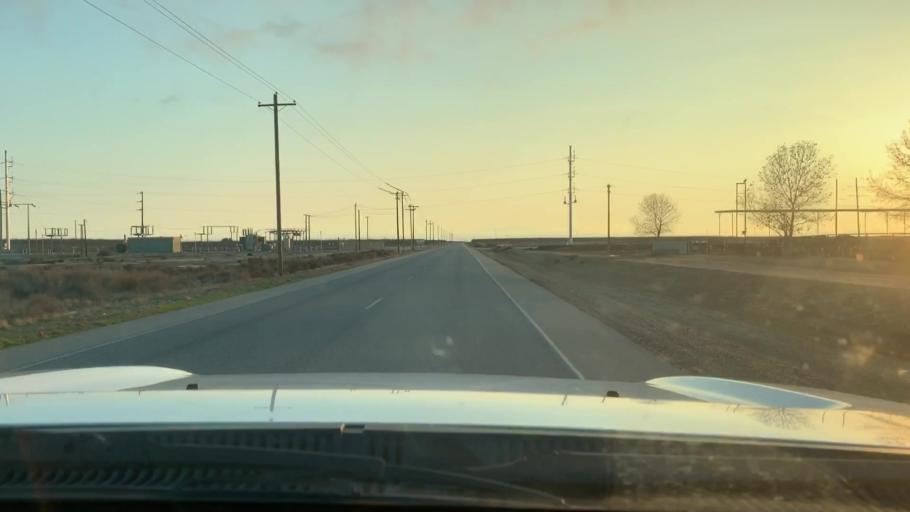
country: US
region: California
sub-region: Kern County
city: Buttonwillow
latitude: 35.5005
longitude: -119.4508
